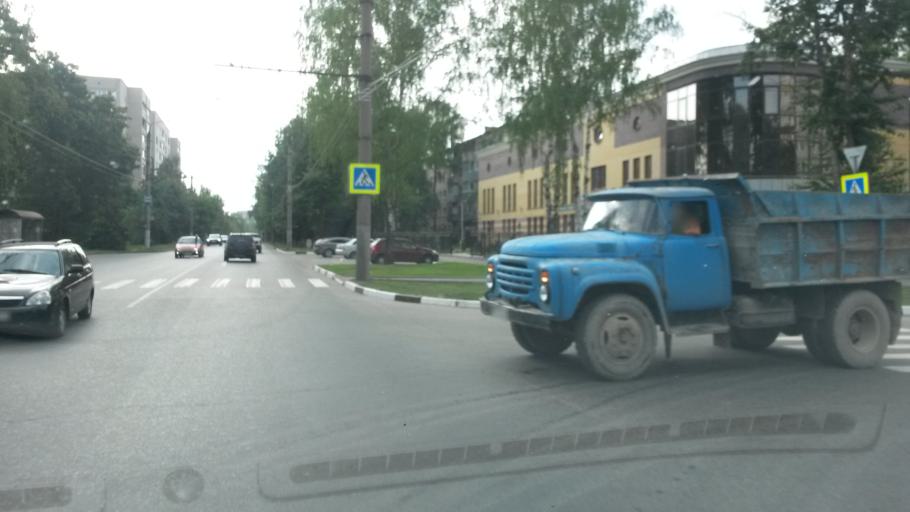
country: RU
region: Ivanovo
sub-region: Gorod Ivanovo
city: Ivanovo
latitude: 57.0061
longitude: 40.9526
